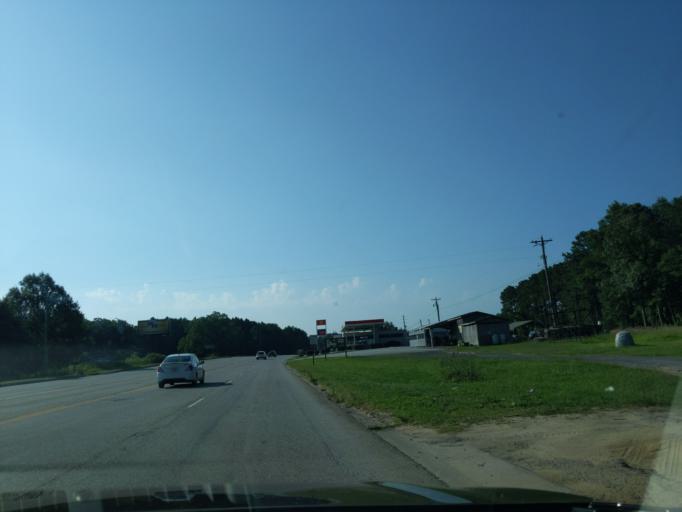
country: US
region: South Carolina
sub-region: Newberry County
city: Prosperity
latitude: 34.2245
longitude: -81.5449
